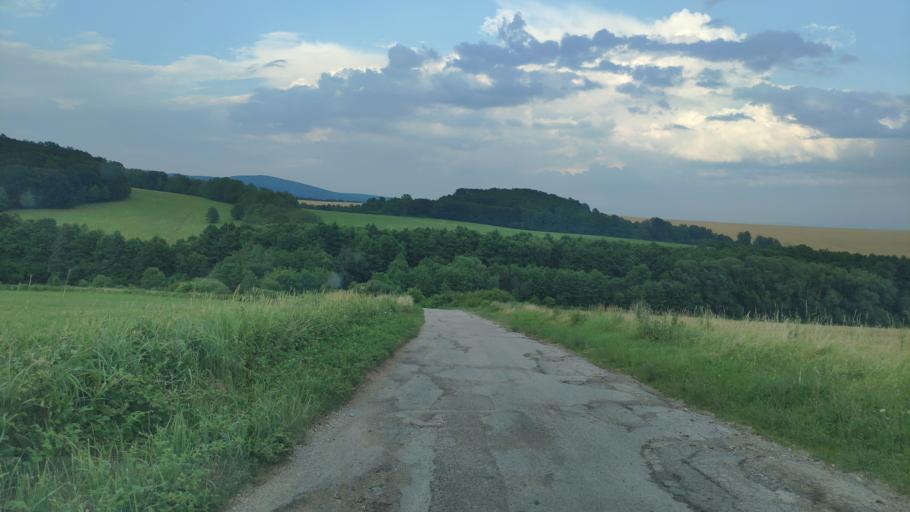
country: SK
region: Kosicky
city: Medzev
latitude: 48.7062
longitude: 20.9819
